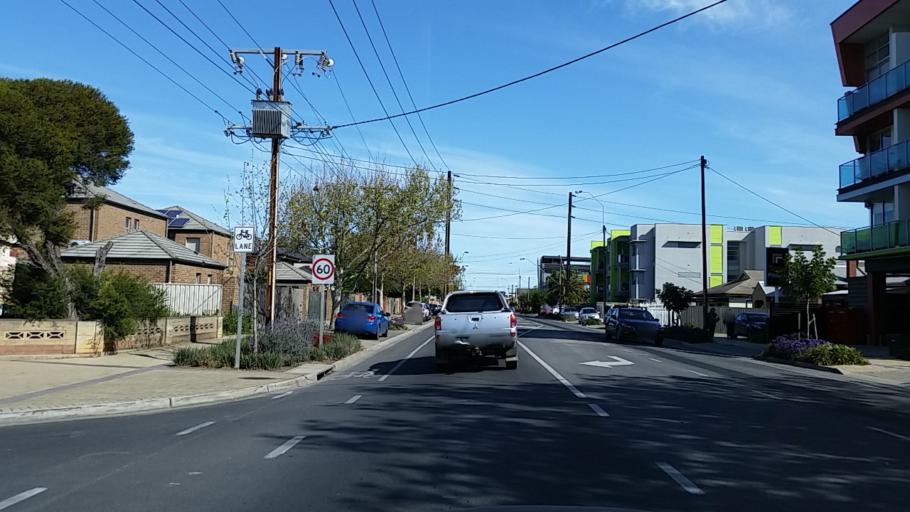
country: AU
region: South Australia
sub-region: Prospect
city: Prospect
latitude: -34.8806
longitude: 138.5846
